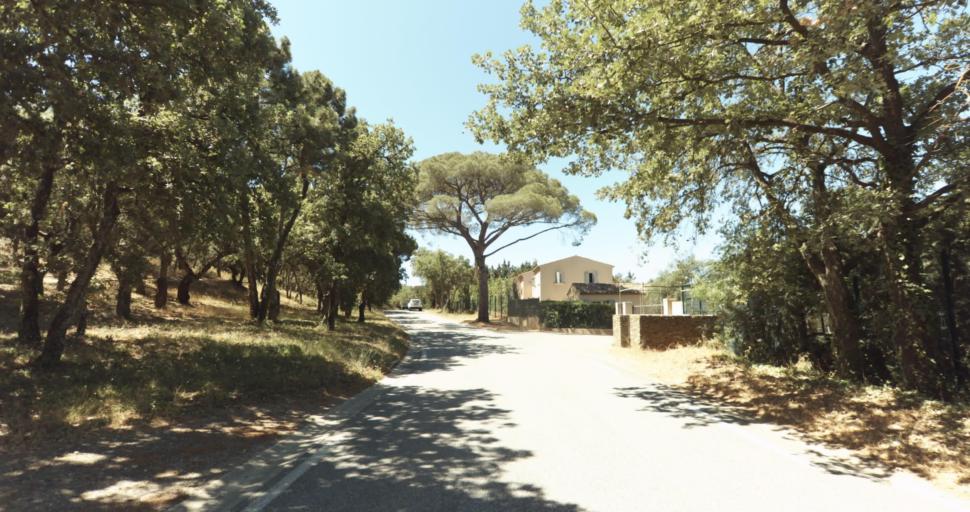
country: FR
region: Provence-Alpes-Cote d'Azur
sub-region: Departement du Var
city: Gassin
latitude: 43.2508
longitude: 6.5818
